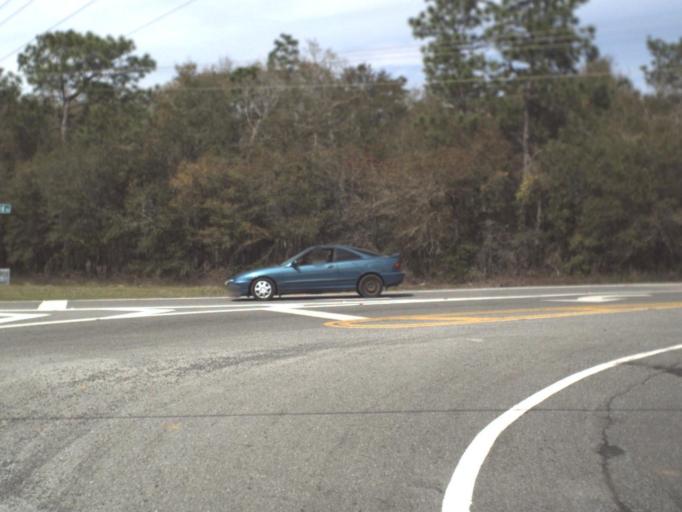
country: US
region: Florida
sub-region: Leon County
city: Tallahassee
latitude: 30.3979
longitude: -84.3374
